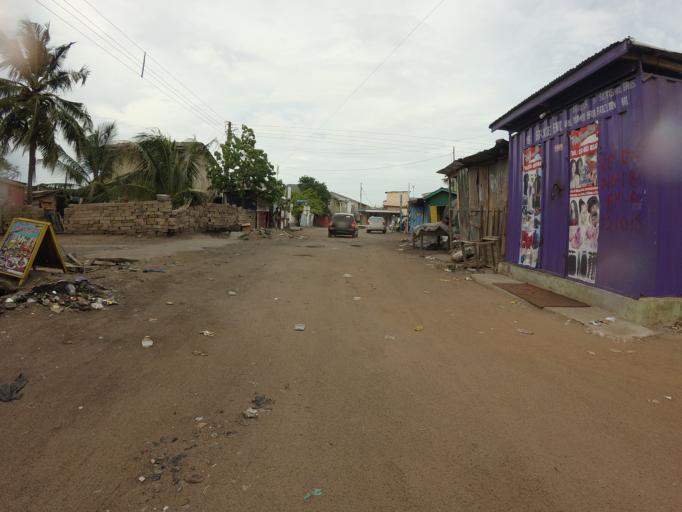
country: GH
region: Greater Accra
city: Accra
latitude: 5.5979
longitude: -0.2174
